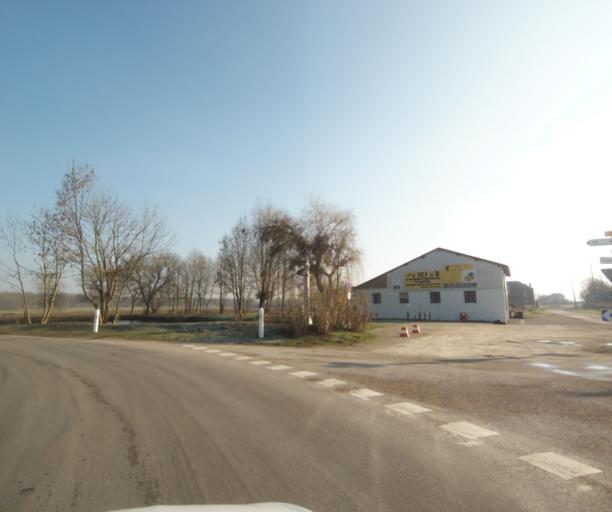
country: FR
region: Champagne-Ardenne
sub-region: Departement de la Haute-Marne
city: Montier-en-Der
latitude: 48.4741
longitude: 4.7847
